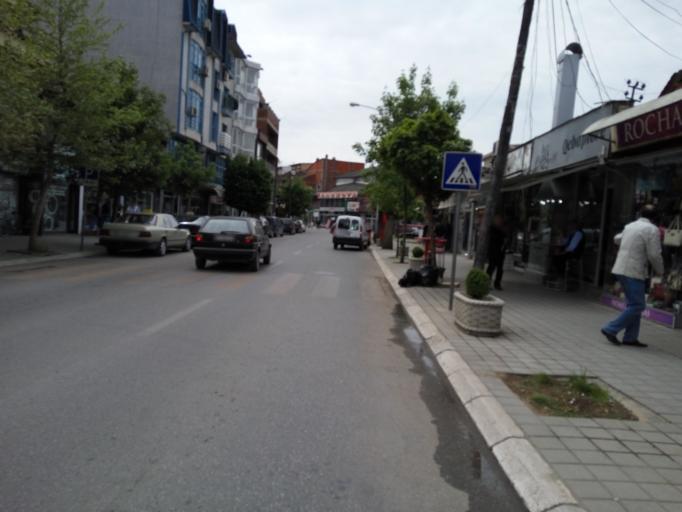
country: XK
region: Gjakova
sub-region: Komuna e Gjakoves
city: Gjakove
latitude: 42.3792
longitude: 20.4310
